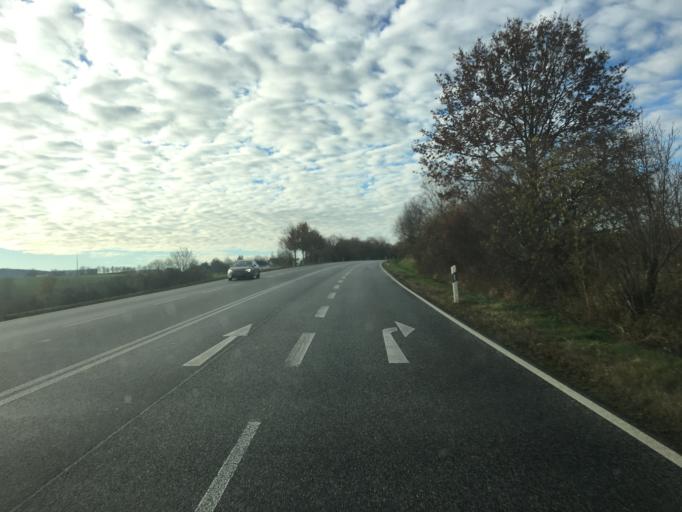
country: DE
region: North Rhine-Westphalia
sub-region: Regierungsbezirk Koln
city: Kall
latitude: 50.5600
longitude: 6.5750
